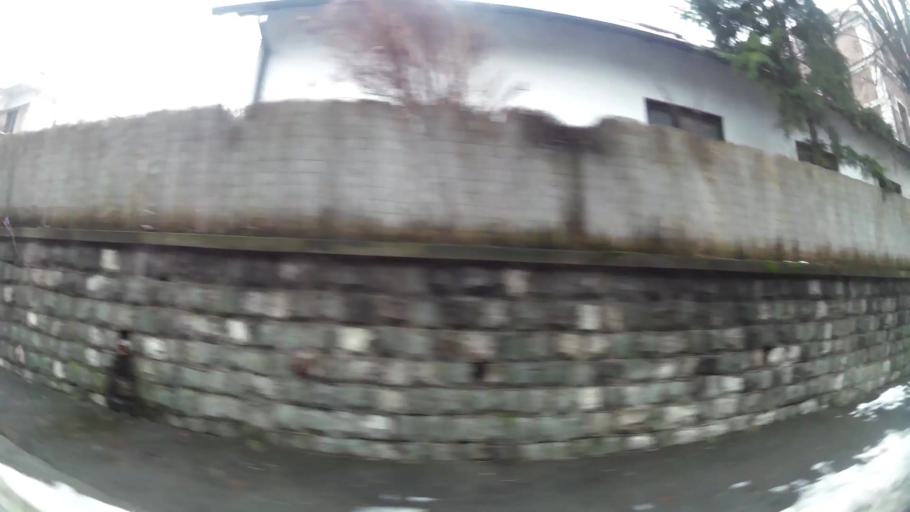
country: RS
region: Central Serbia
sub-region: Belgrade
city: Cukarica
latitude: 44.7912
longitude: 20.4343
